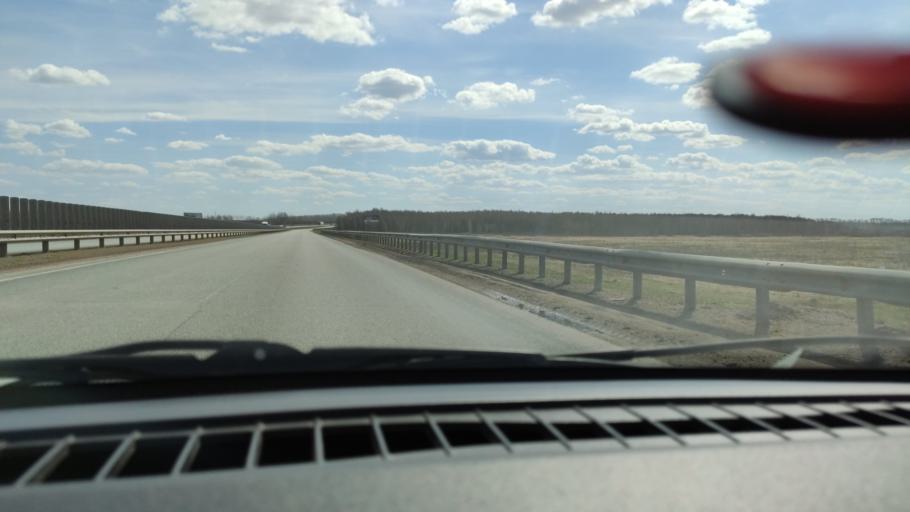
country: RU
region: Bashkortostan
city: Asanovo
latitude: 54.9666
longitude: 55.5814
